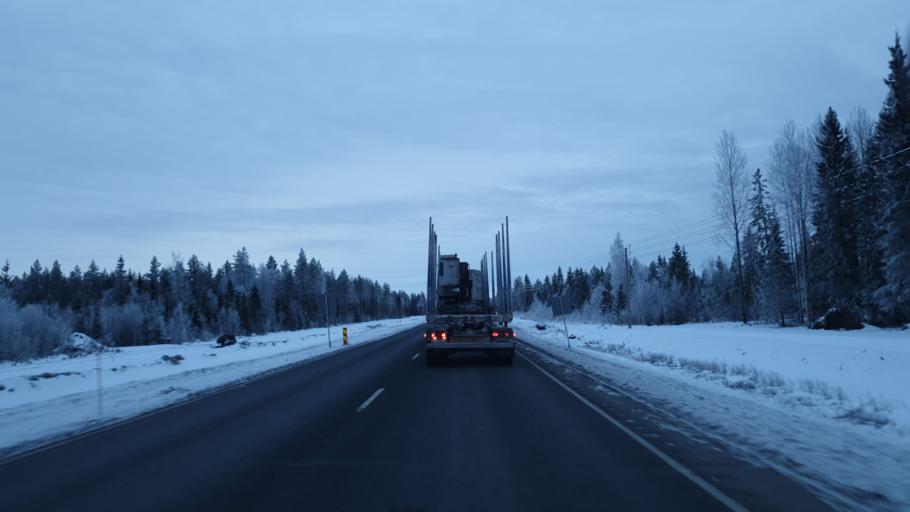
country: FI
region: Northern Ostrobothnia
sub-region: Oulunkaari
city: Ii
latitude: 65.3876
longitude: 25.3791
